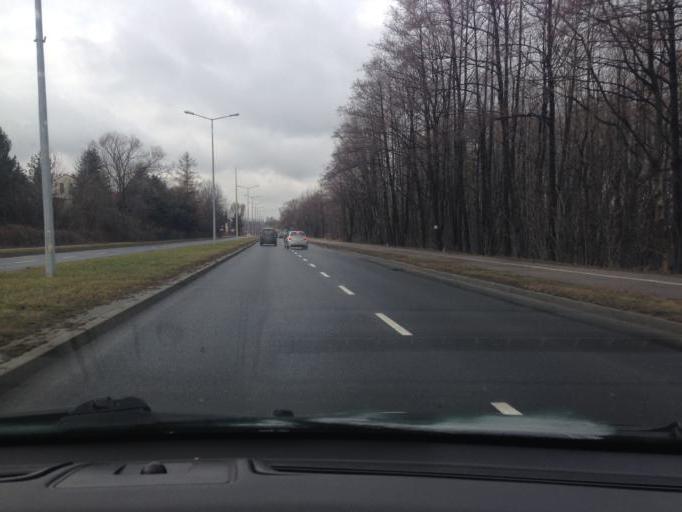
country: PL
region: Silesian Voivodeship
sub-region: Bielsko-Biala
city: Bielsko-Biala
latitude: 49.7942
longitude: 19.0570
